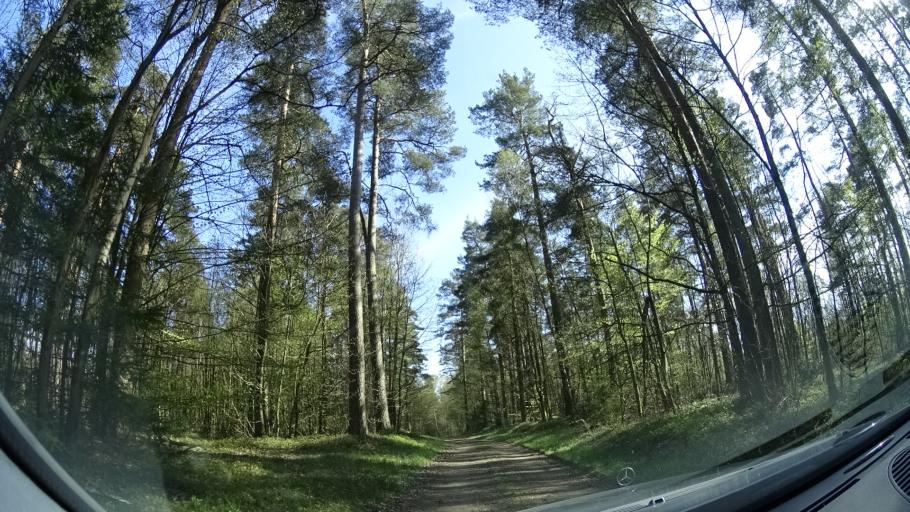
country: SE
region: Skane
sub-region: Hassleholms Kommun
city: Tormestorp
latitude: 56.1014
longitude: 13.6699
